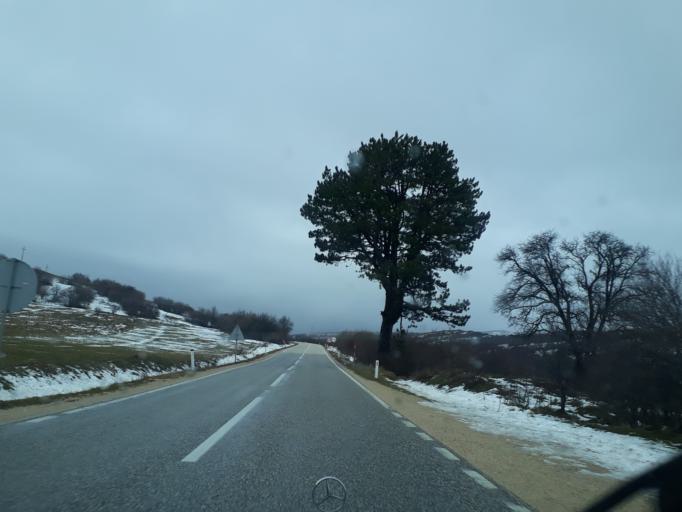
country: BA
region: Federation of Bosnia and Herzegovina
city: Tomislavgrad
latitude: 43.8098
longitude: 17.2036
